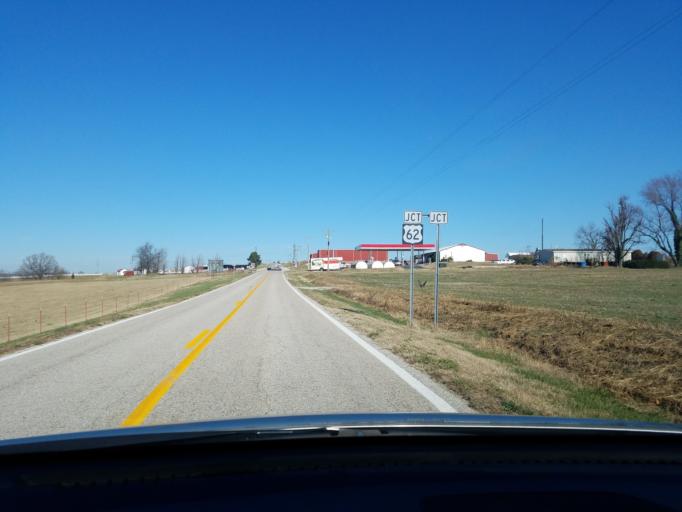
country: US
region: Arkansas
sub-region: Carroll County
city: Berryville
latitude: 36.3884
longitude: -93.6216
